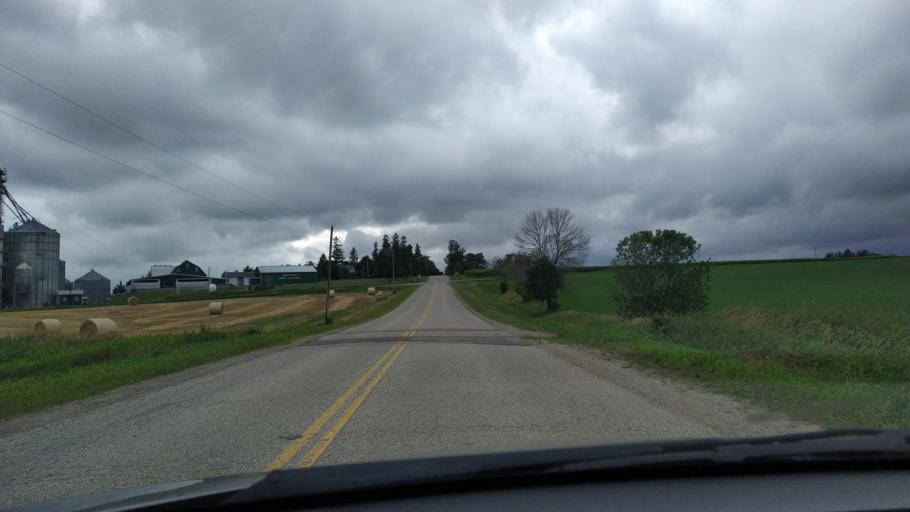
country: CA
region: Ontario
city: Kitchener
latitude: 43.3359
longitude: -80.6242
